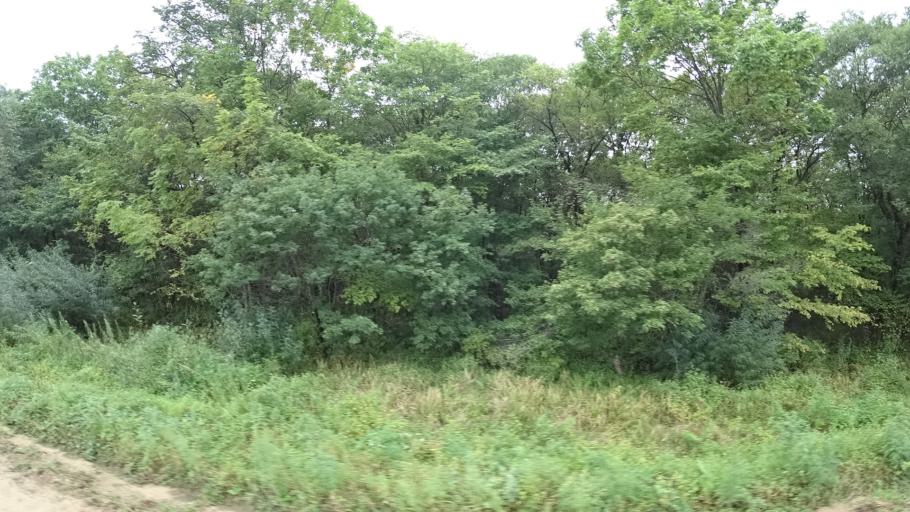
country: RU
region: Primorskiy
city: Rettikhovka
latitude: 44.0615
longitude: 132.6541
